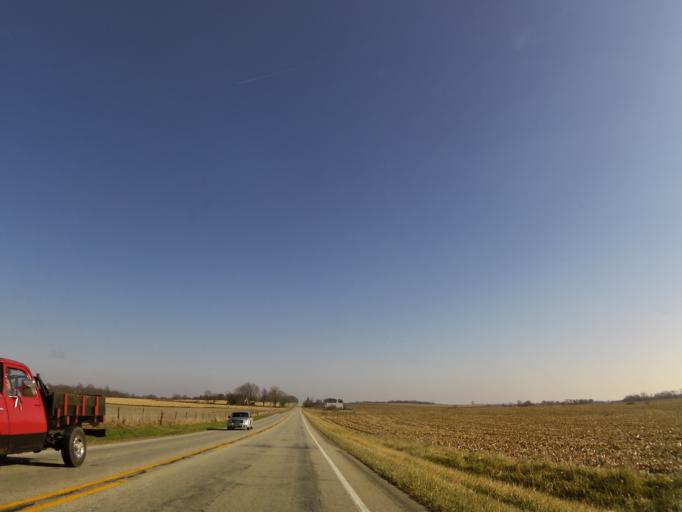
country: US
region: Indiana
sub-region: Fayette County
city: Connersville
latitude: 39.6287
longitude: -85.2562
